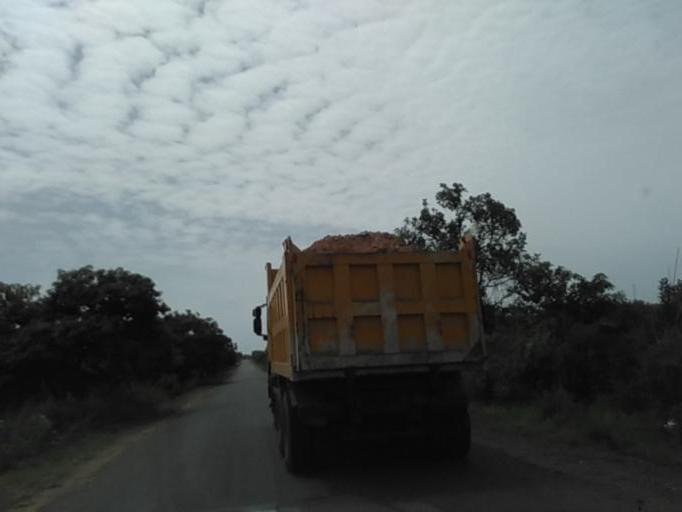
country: GH
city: Akropong
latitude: 6.0933
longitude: 0.0625
